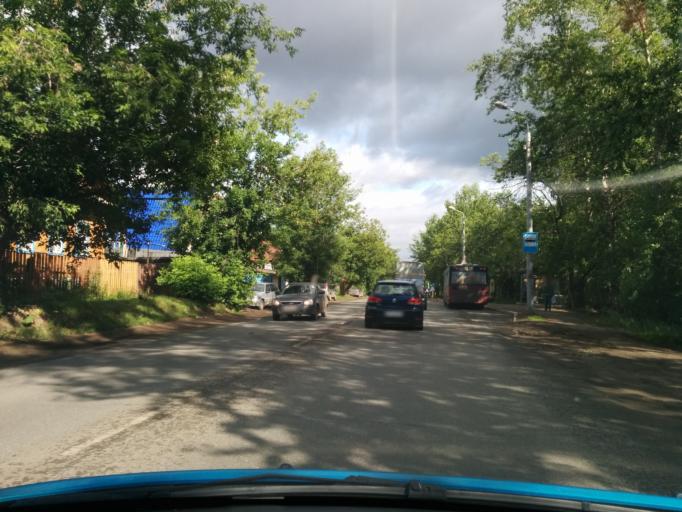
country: RU
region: Perm
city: Kondratovo
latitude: 58.0436
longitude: 56.1023
